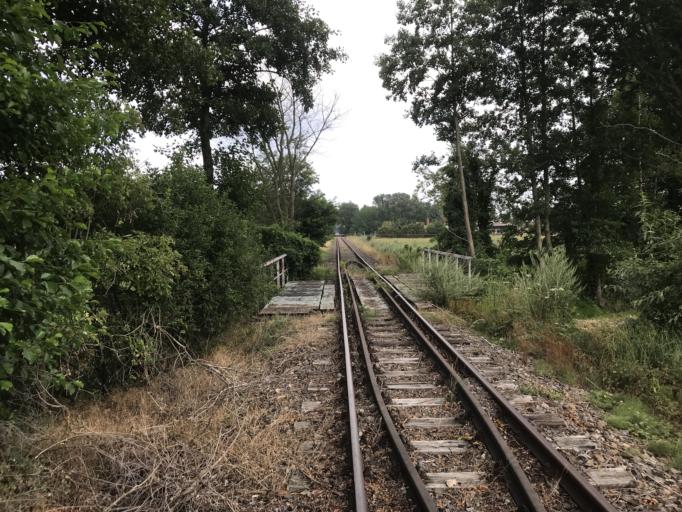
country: DE
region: Brandenburg
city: Sperenberg
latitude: 52.0799
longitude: 13.3118
